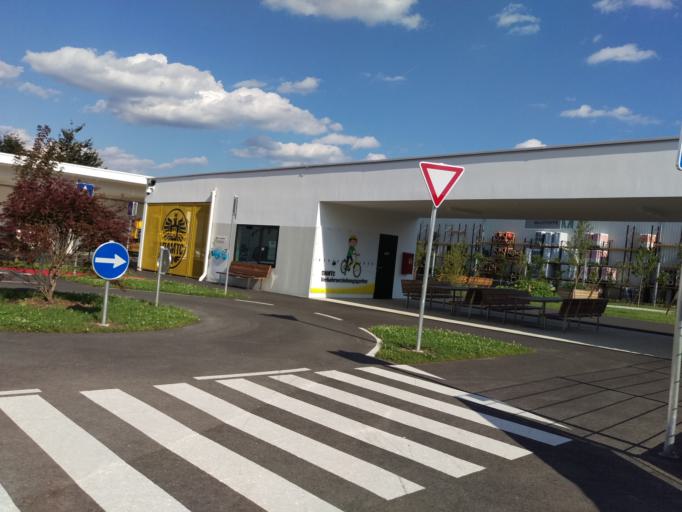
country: AT
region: Styria
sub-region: Graz Stadt
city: Wetzelsdorf
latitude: 47.0660
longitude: 15.4134
